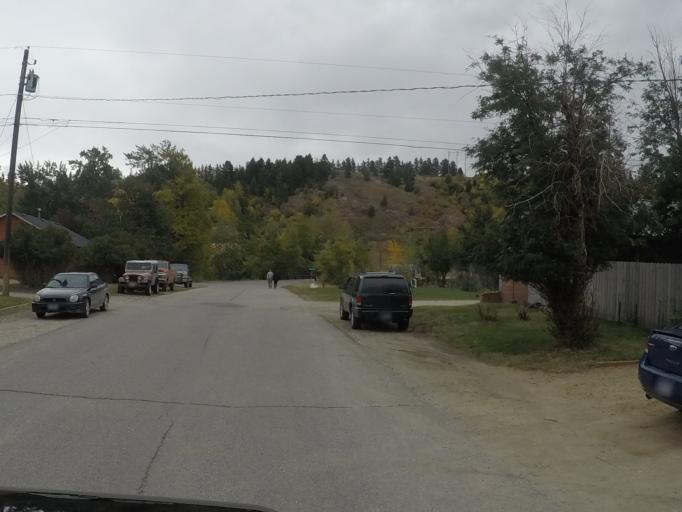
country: US
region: Montana
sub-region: Carbon County
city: Red Lodge
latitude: 45.1889
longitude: -109.2442
